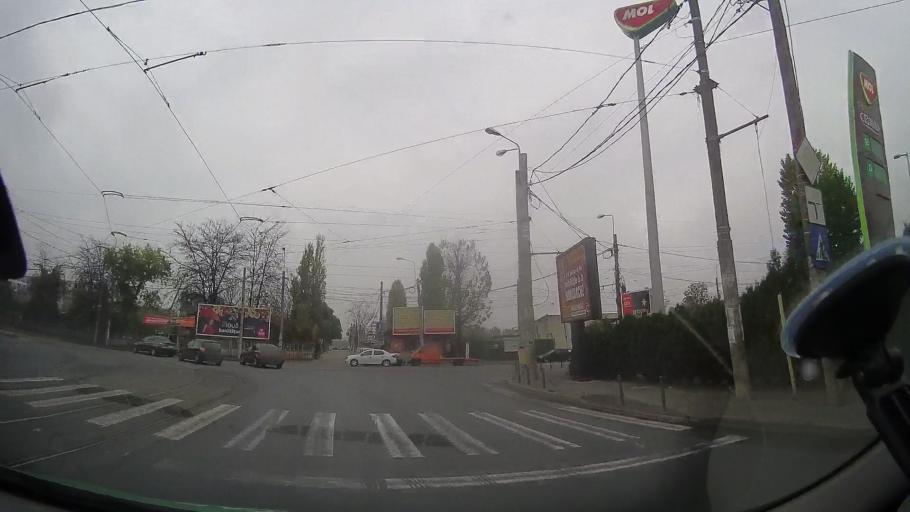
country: RO
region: Ilfov
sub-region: Comuna Chiajna
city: Rosu
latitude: 44.4239
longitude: 25.9999
